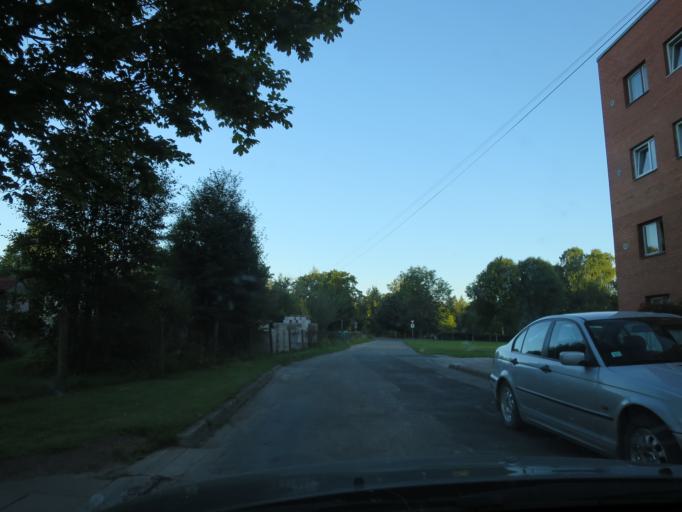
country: LV
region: Sigulda
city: Sigulda
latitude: 57.1600
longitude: 24.8552
